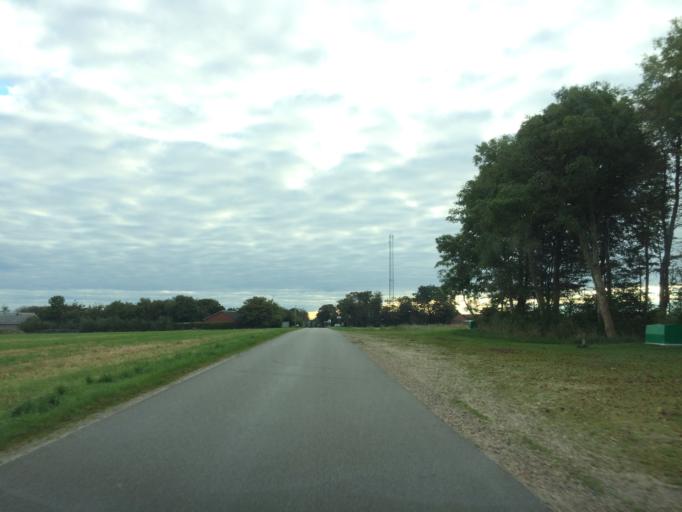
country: DK
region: Central Jutland
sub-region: Ringkobing-Skjern Kommune
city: Skjern
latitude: 56.0571
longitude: 8.4988
